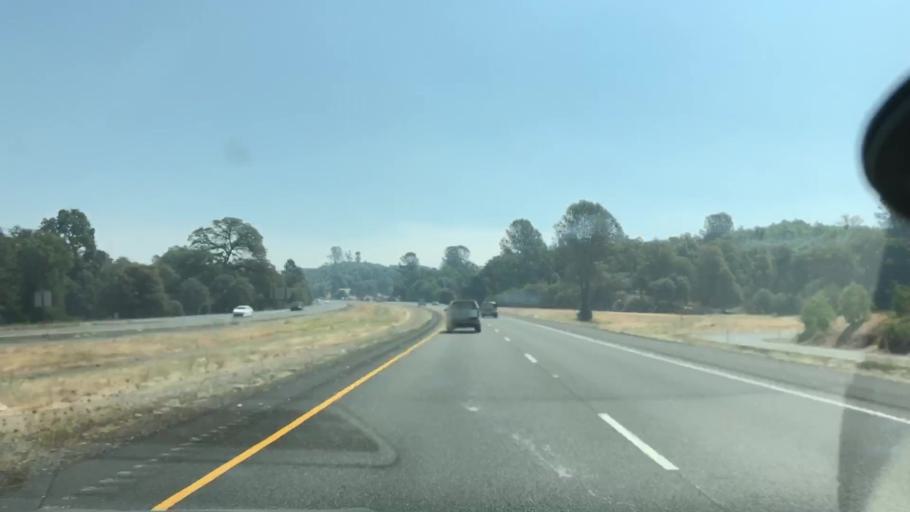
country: US
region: California
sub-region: El Dorado County
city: Shingle Springs
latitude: 38.6958
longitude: -120.8859
